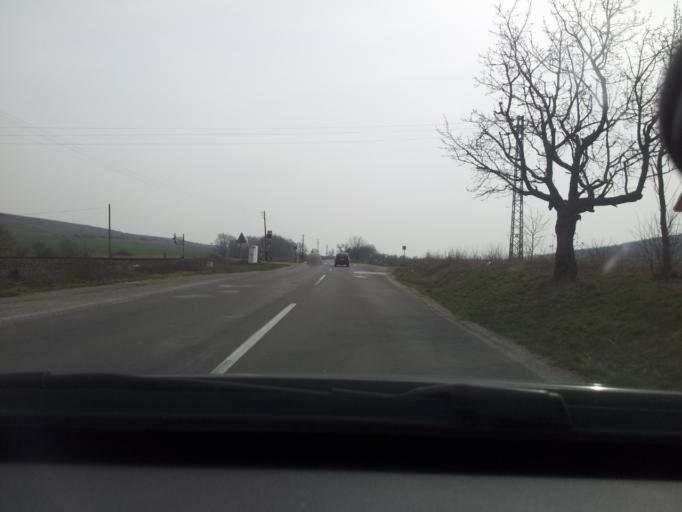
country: SK
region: Trnavsky
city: Hlohovec
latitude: 48.4149
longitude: 17.8310
